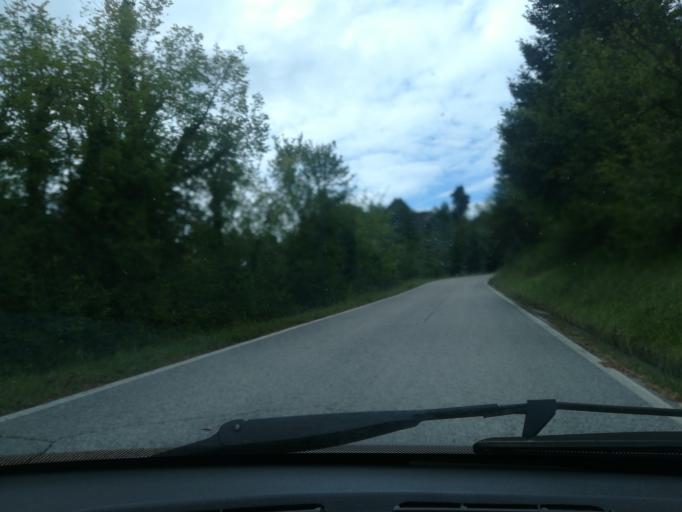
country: IT
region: The Marches
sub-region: Province of Fermo
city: Montefortino
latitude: 42.9388
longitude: 13.3723
